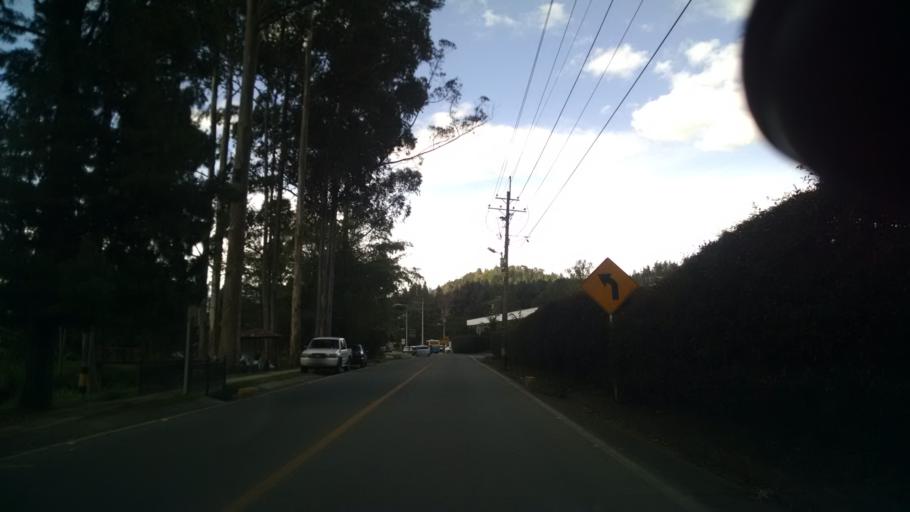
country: CO
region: Antioquia
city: El Retiro
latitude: 6.0714
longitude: -75.4988
